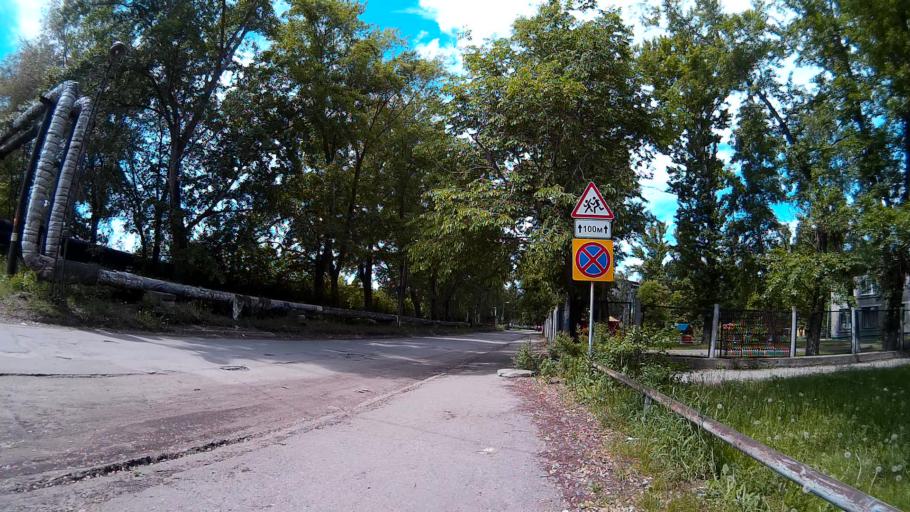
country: RU
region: Ulyanovsk
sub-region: Ulyanovskiy Rayon
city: Ulyanovsk
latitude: 54.2868
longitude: 48.3672
